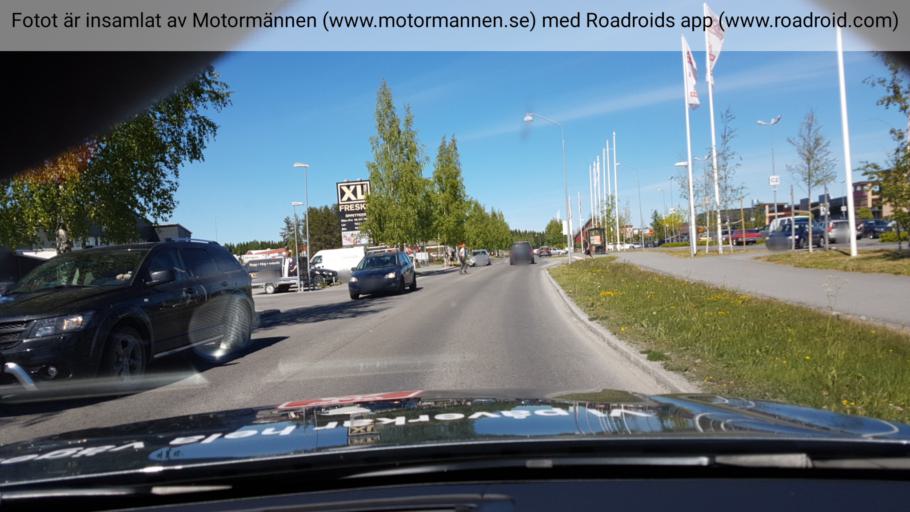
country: SE
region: Jaemtland
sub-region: OEstersunds Kommun
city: Ostersund
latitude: 63.1702
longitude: 14.6899
